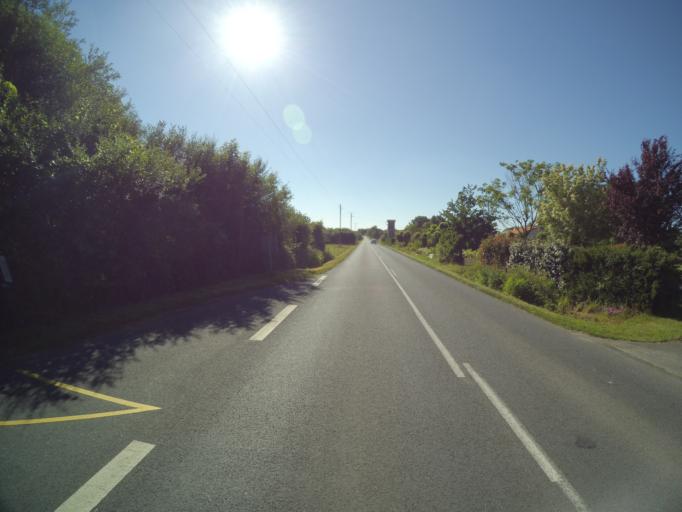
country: FR
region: Pays de la Loire
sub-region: Departement de la Vendee
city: La Guyonniere
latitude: 46.9555
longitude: -1.2264
